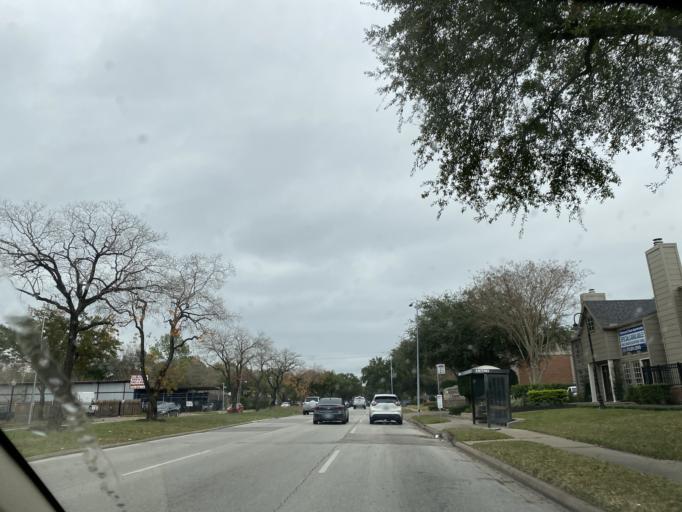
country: US
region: Texas
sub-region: Harris County
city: Piney Point Village
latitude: 29.7292
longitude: -95.5121
